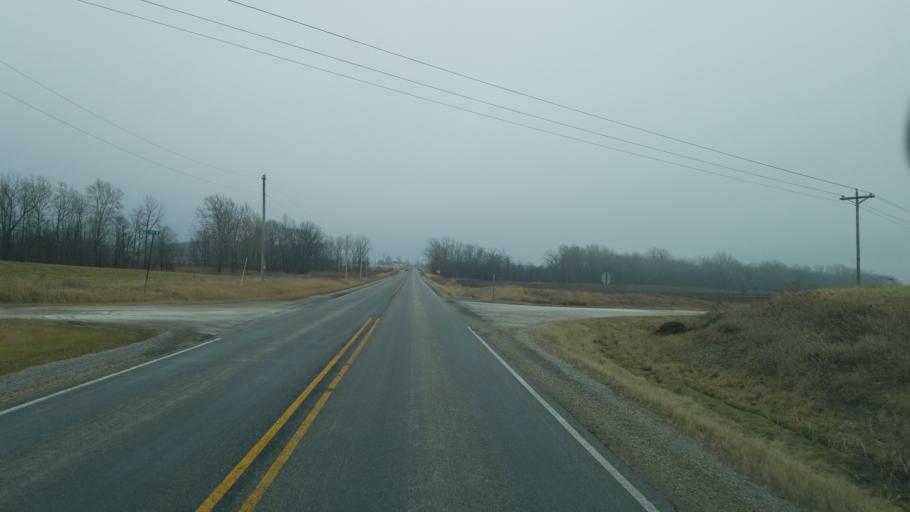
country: US
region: Indiana
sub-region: Adams County
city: Geneva
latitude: 40.5464
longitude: -85.0021
